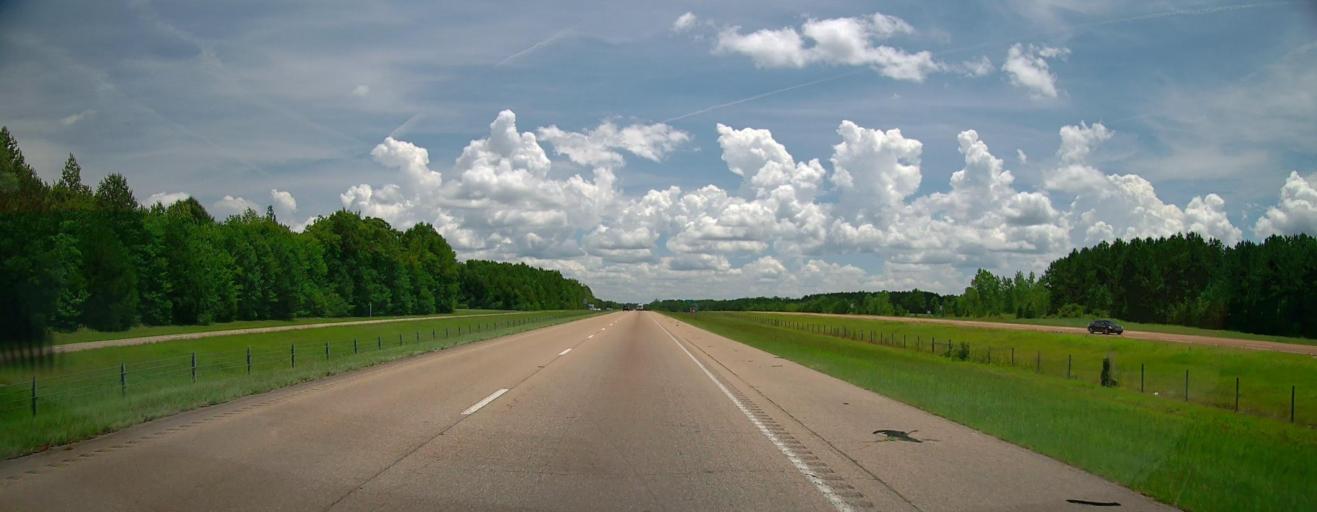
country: US
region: Mississippi
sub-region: Lee County
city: Saltillo
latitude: 34.3665
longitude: -88.8579
